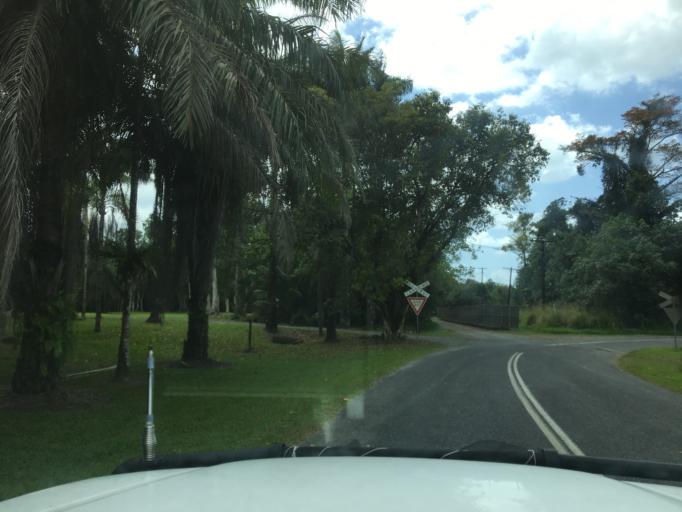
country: AU
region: Queensland
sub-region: Cairns
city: Woree
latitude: -17.2167
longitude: 145.9178
